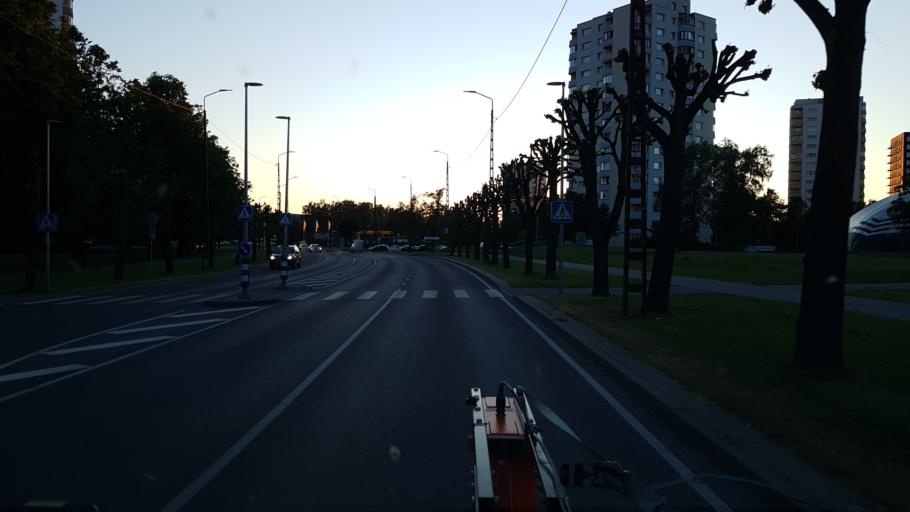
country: EE
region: Harju
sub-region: Saue vald
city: Laagri
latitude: 59.4189
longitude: 24.6498
